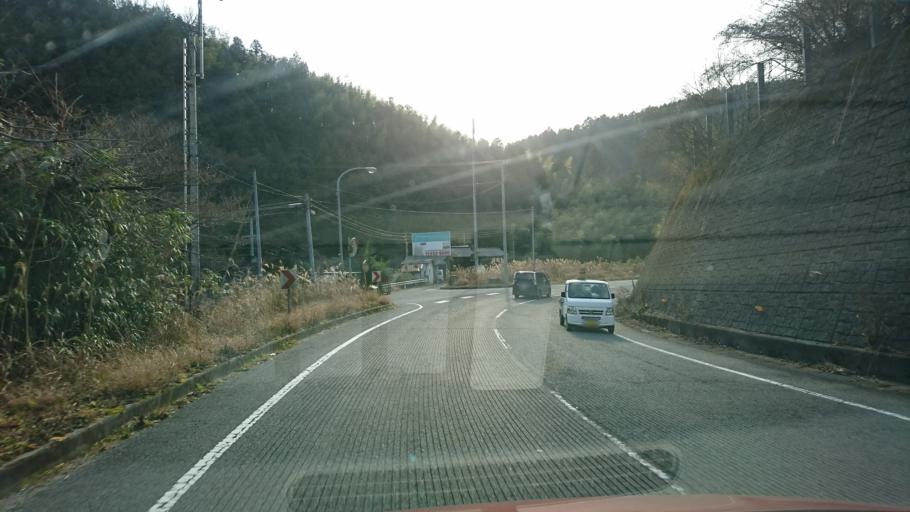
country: JP
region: Ehime
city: Hojo
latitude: 33.9175
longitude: 132.8851
